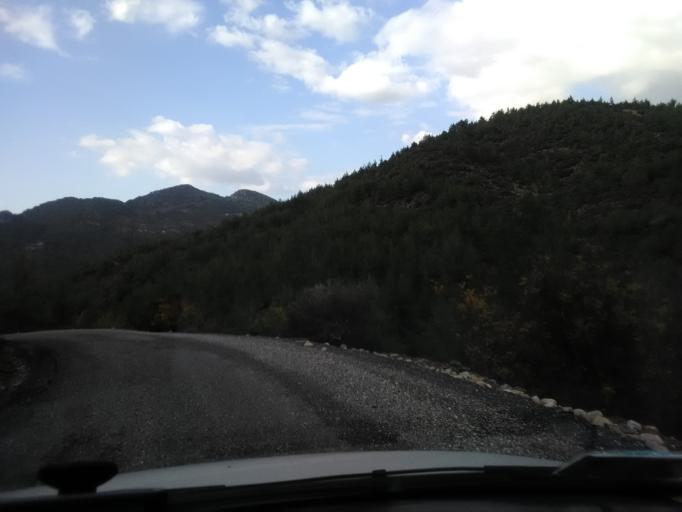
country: TR
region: Antalya
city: Gazipasa
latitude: 36.3029
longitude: 32.3902
